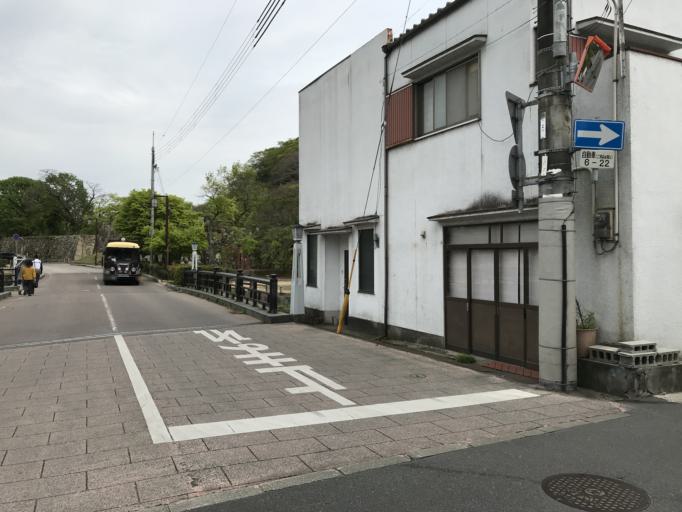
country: JP
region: Hyogo
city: Himeji
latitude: 34.8408
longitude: 134.6915
